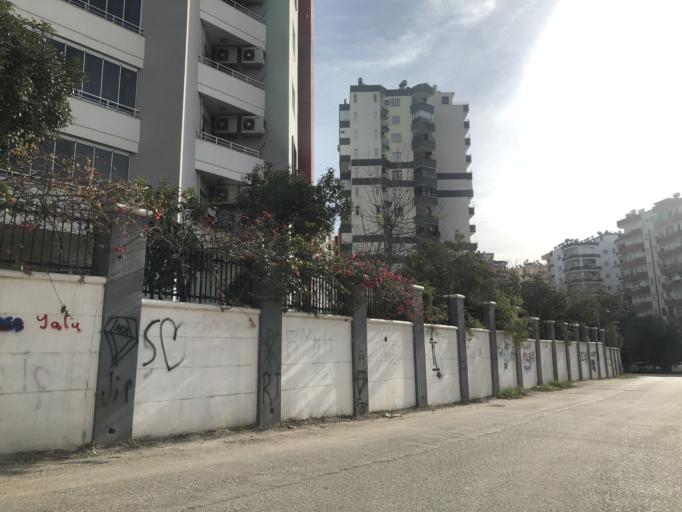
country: TR
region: Adana
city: Adana
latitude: 37.0524
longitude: 35.2876
